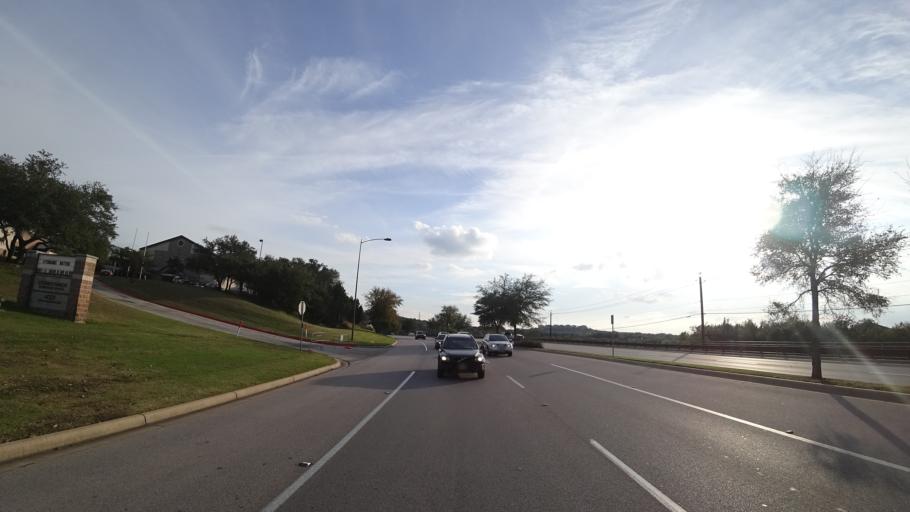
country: US
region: Texas
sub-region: Travis County
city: Hudson Bend
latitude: 30.3802
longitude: -97.8849
